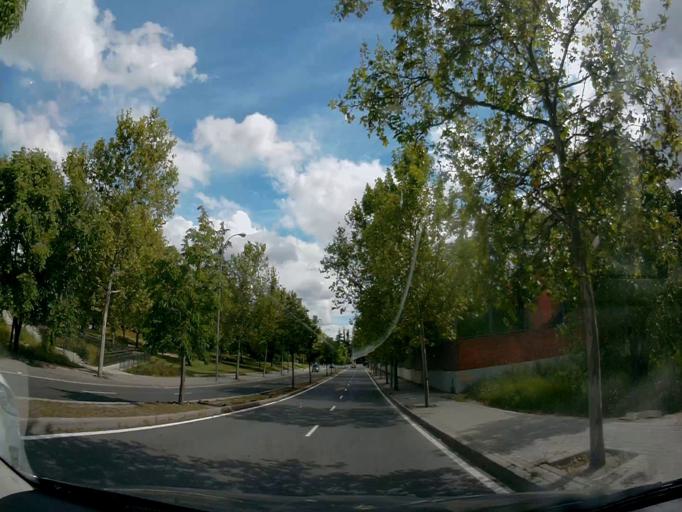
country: ES
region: Madrid
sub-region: Provincia de Madrid
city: Vicalvaro
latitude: 40.4112
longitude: -3.6100
